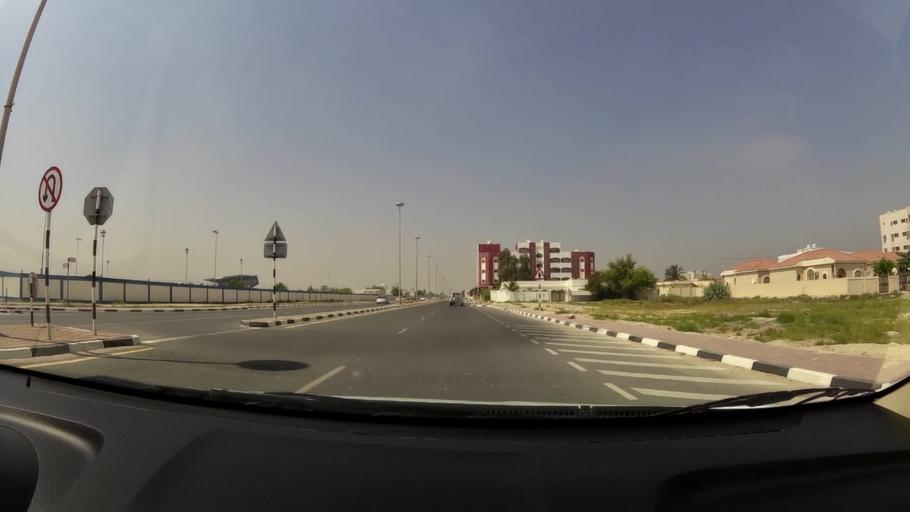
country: AE
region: Umm al Qaywayn
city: Umm al Qaywayn
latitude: 25.5689
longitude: 55.5591
